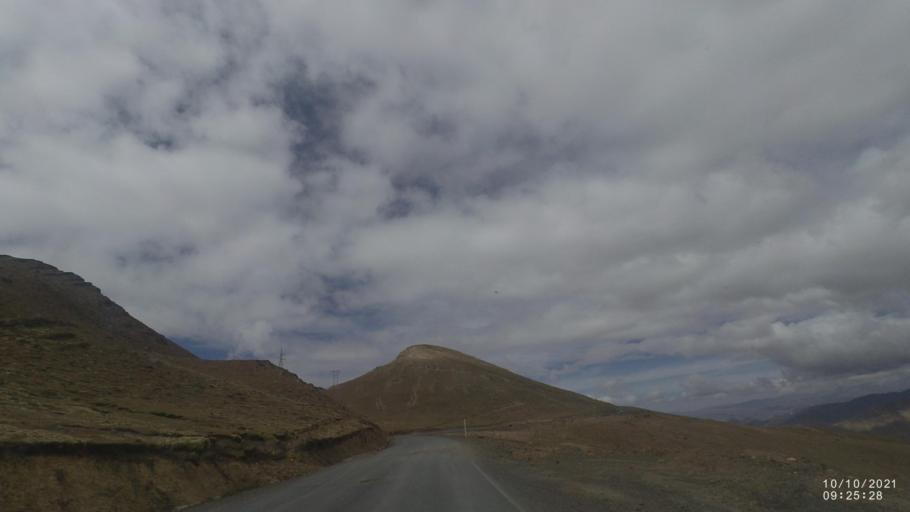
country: BO
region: La Paz
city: Quime
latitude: -17.0912
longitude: -67.3163
